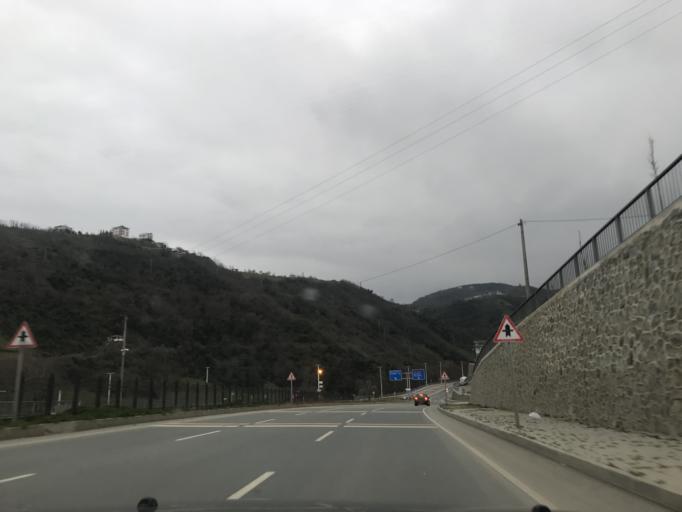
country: TR
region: Trabzon
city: Akcaabat
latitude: 41.0016
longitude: 39.6269
